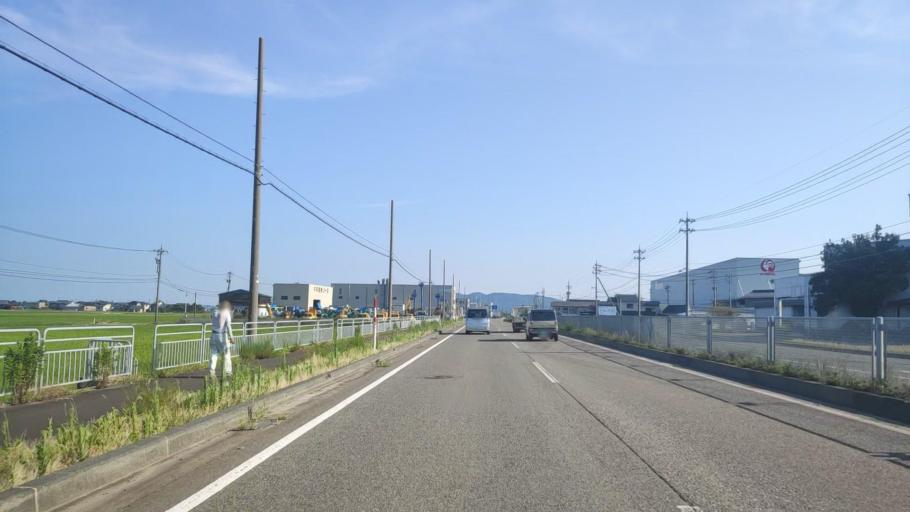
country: JP
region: Fukui
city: Maruoka
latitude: 36.1641
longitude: 136.2636
